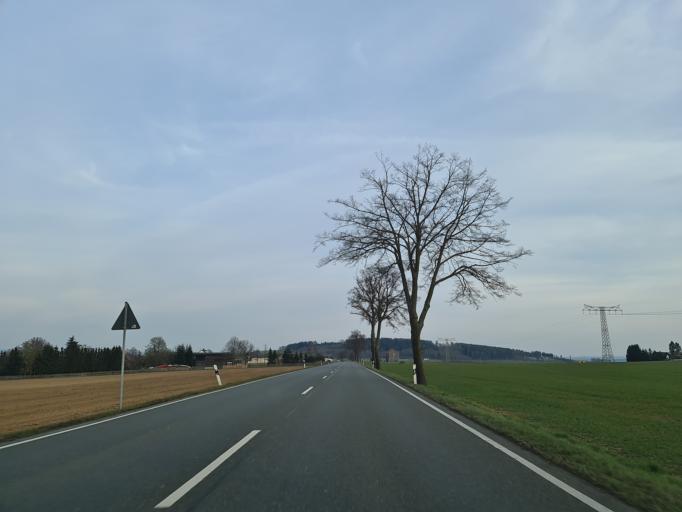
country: DE
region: Saxony
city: Plauen
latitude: 50.4605
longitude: 12.1568
